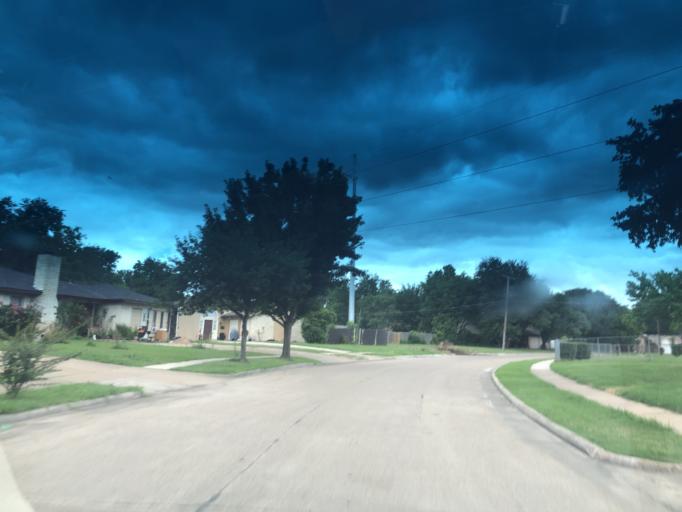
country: US
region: Texas
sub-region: Dallas County
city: Grand Prairie
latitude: 32.7041
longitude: -97.0107
